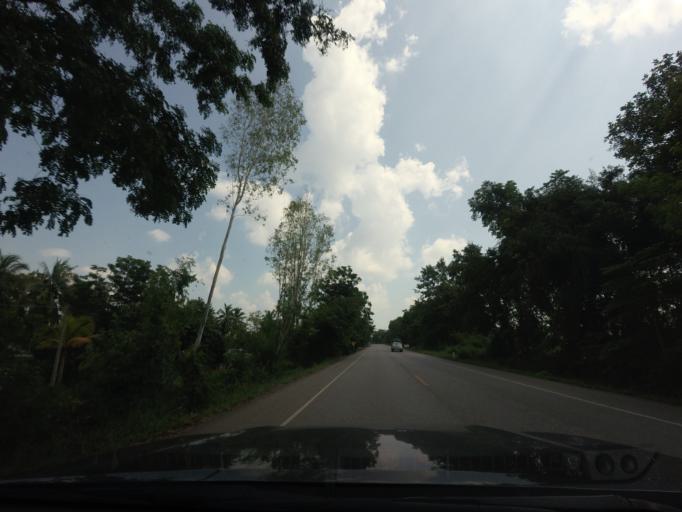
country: TH
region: Phitsanulok
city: Chat Trakan
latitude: 17.2703
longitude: 100.5457
